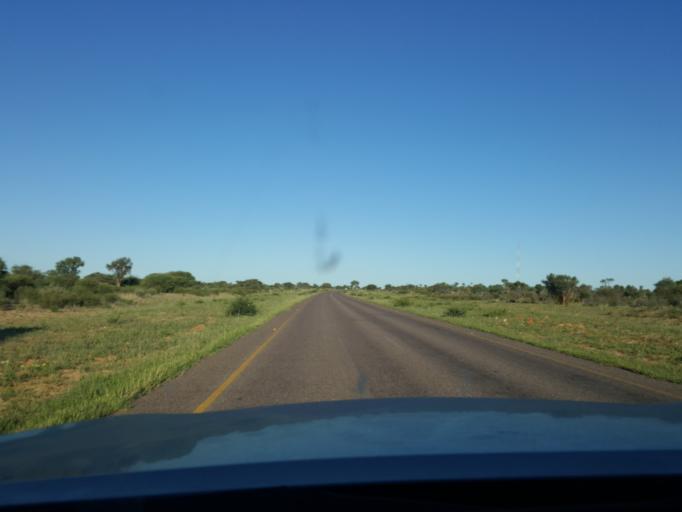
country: BW
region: Southern
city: Khakhea
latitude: -24.3031
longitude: 23.3972
